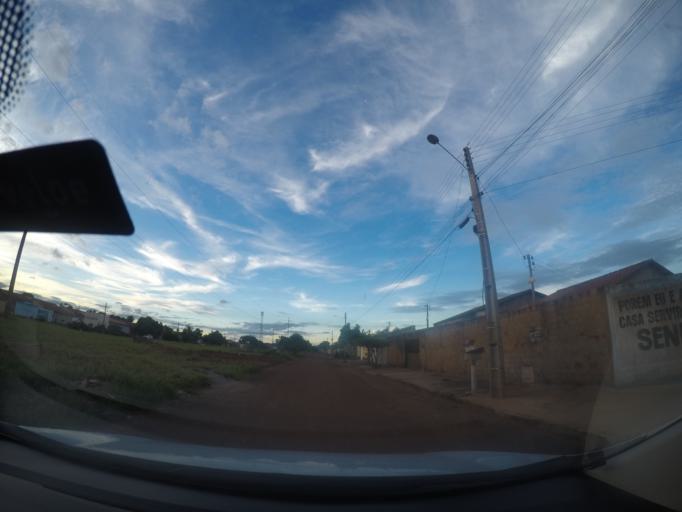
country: BR
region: Goias
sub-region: Goianira
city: Goianira
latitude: -16.5763
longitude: -49.3805
